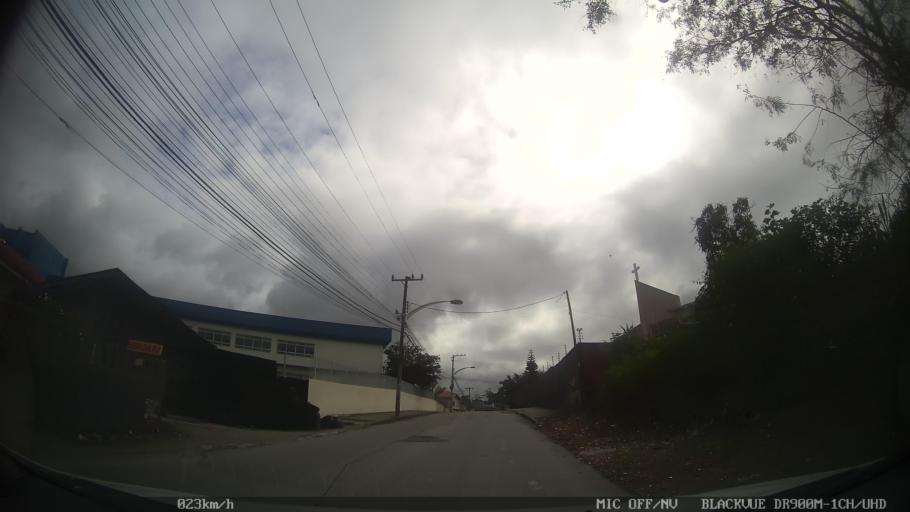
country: BR
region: Santa Catarina
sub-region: Biguacu
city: Biguacu
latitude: -27.5378
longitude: -48.6469
